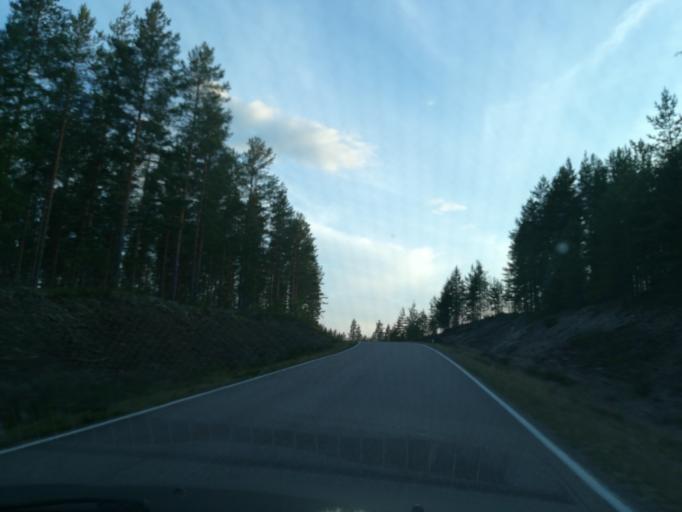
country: FI
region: South Karelia
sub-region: Lappeenranta
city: Joutseno
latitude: 61.3495
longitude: 28.4441
